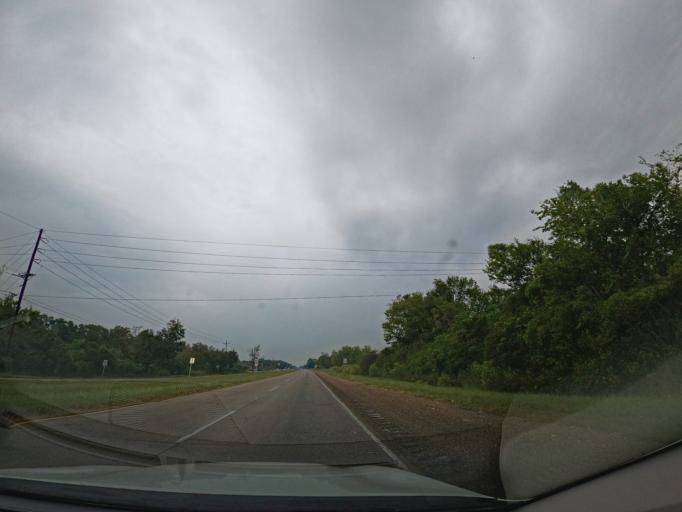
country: US
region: Louisiana
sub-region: Iberia Parish
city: New Iberia
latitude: 29.9854
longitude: -91.8644
